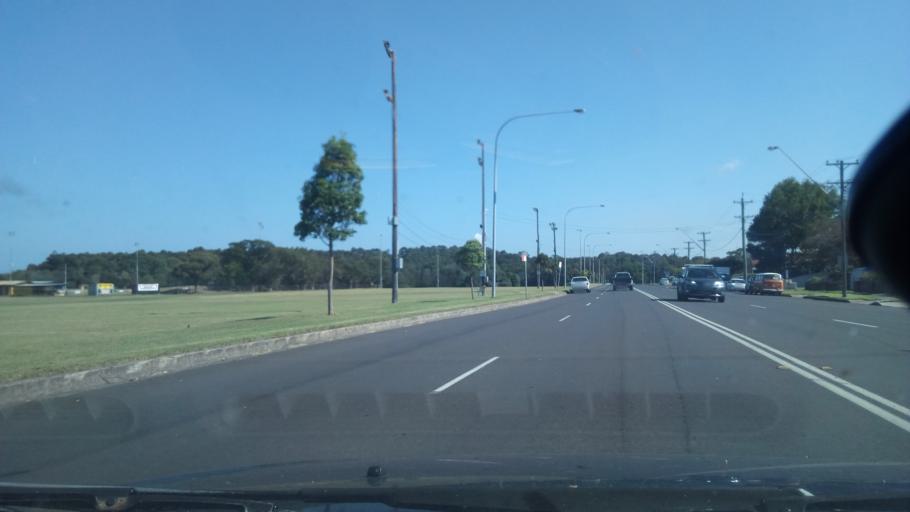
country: AU
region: New South Wales
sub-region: Wollongong
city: Wollongong
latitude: -34.4358
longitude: 150.8919
